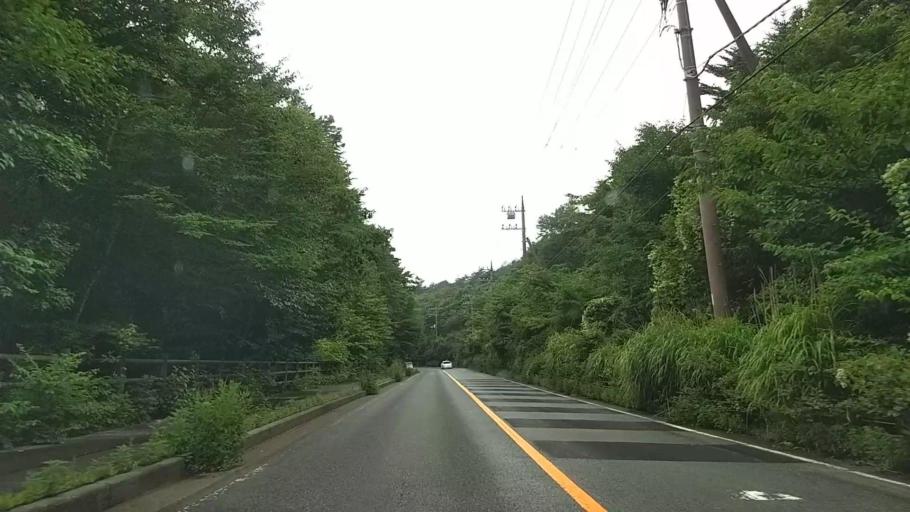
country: JP
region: Yamanashi
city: Fujikawaguchiko
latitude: 35.4861
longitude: 138.6372
